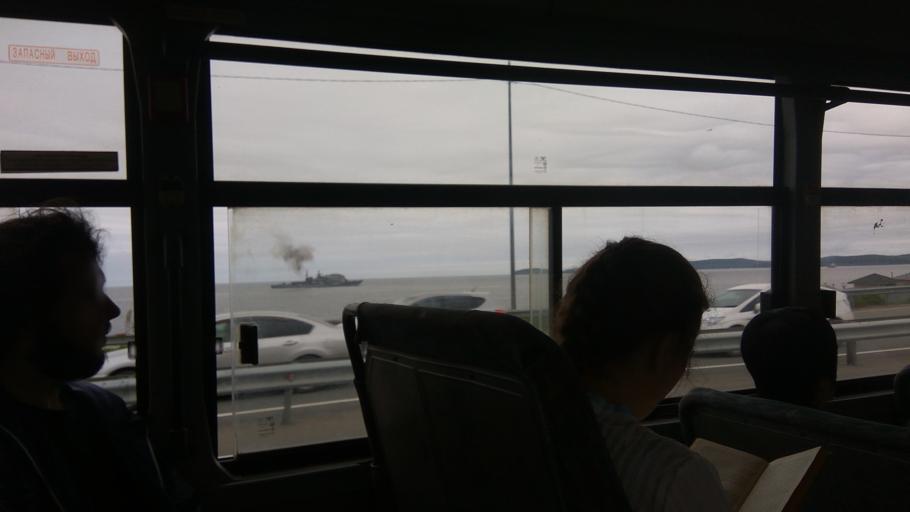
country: RU
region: Primorskiy
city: Vladivostok
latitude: 43.0720
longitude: 131.9394
